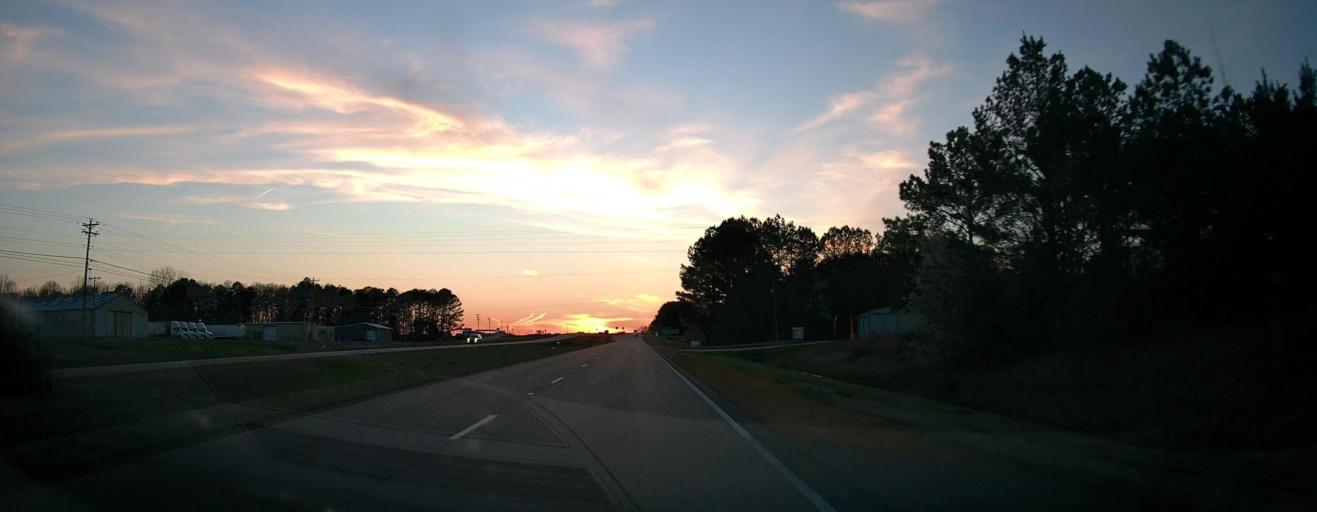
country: US
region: Mississippi
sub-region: Tippah County
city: Ripley
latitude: 34.9524
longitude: -88.8944
